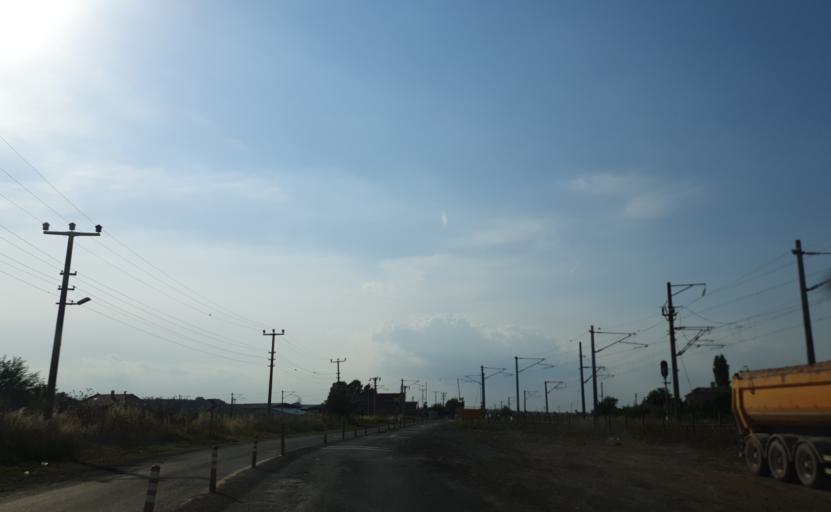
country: TR
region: Tekirdag
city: Muratli
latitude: 41.1773
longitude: 27.4899
